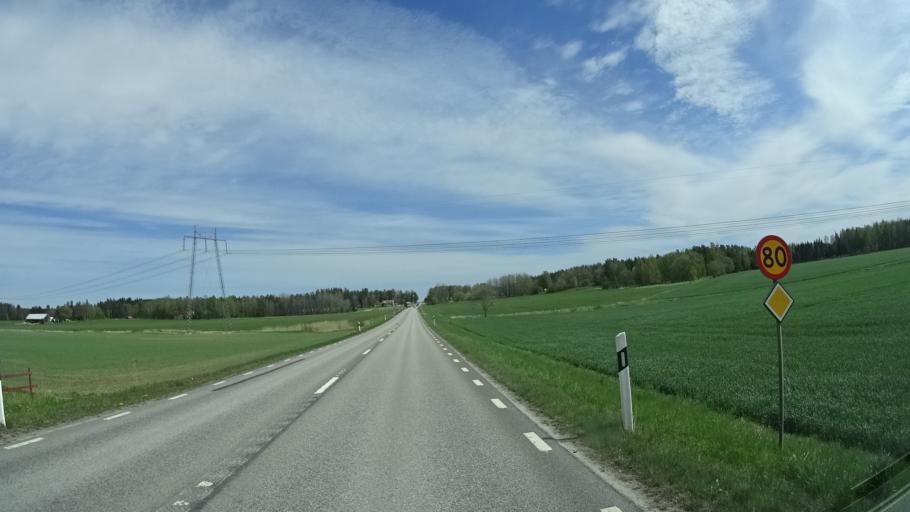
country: SE
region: OEstergoetland
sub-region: Mjolby Kommun
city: Mantorp
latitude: 58.3690
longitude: 15.3318
